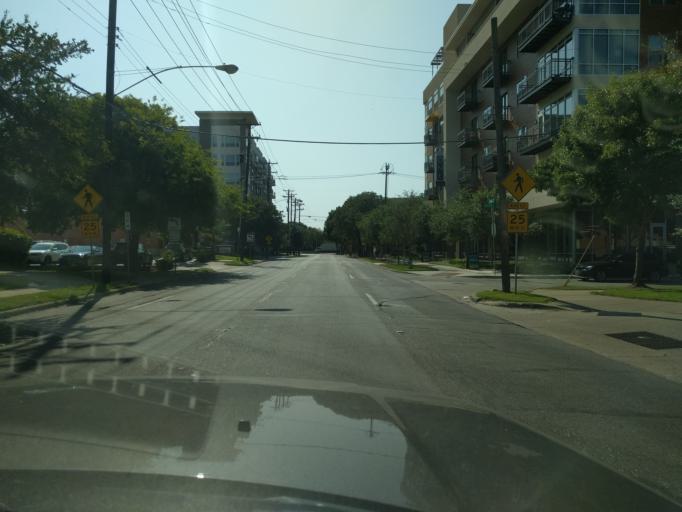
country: US
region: Texas
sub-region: Dallas County
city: Dallas
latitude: 32.8052
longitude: -96.7977
